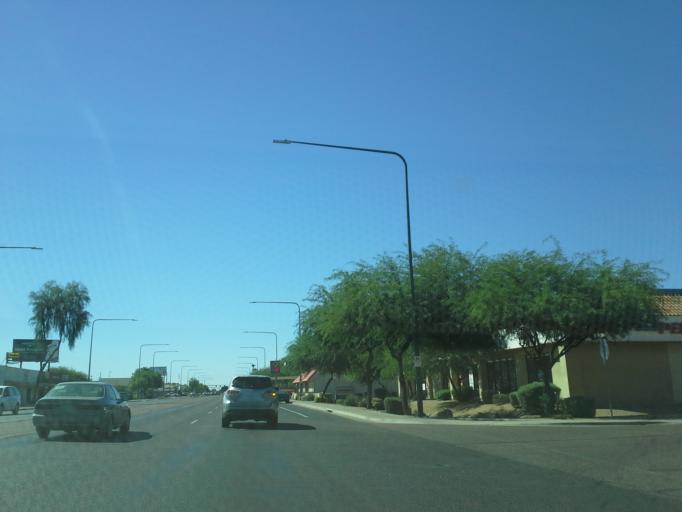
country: US
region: Arizona
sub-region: Maricopa County
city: Chandler
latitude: 33.2973
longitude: -111.8417
